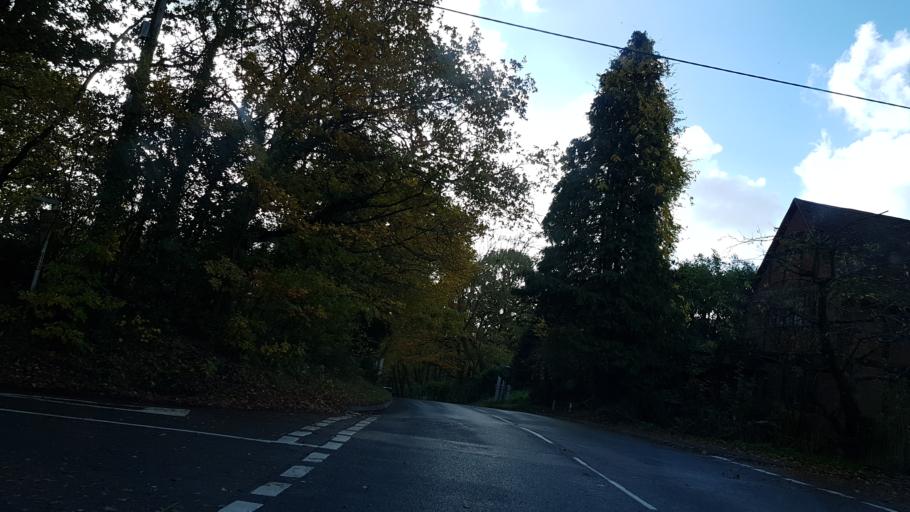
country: GB
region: England
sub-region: Surrey
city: Milford
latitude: 51.1322
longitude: -0.6730
